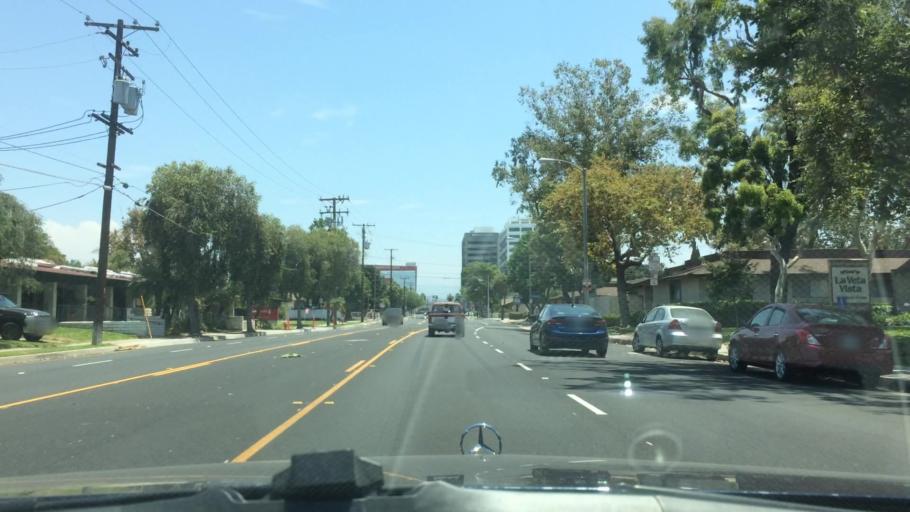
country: US
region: California
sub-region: Orange County
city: Orange
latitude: 33.7803
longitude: -117.8728
